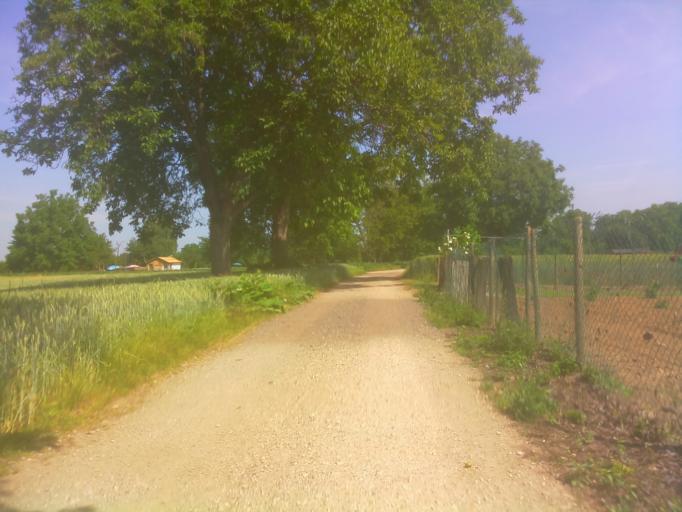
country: DE
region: Baden-Wuerttemberg
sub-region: Karlsruhe Region
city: Weinheim
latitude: 49.5517
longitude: 8.6452
